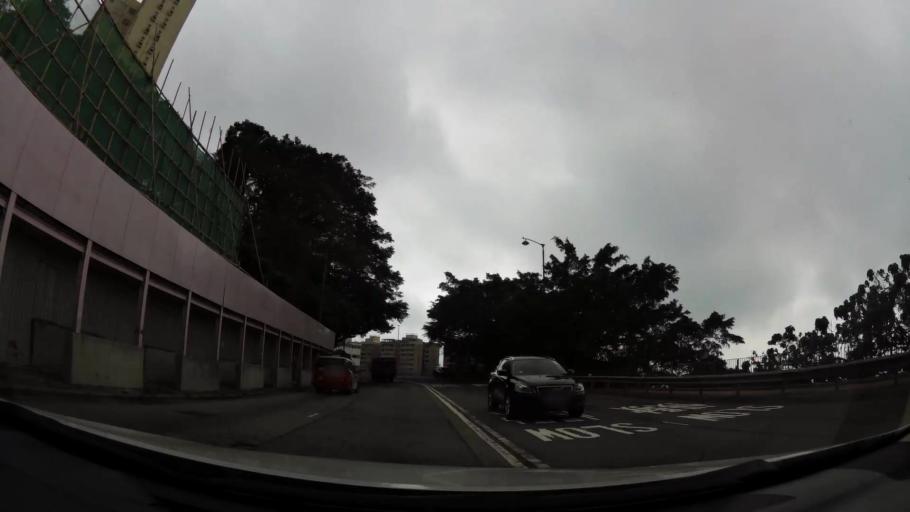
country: HK
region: Central and Western
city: Central
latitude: 22.2651
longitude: 114.1333
